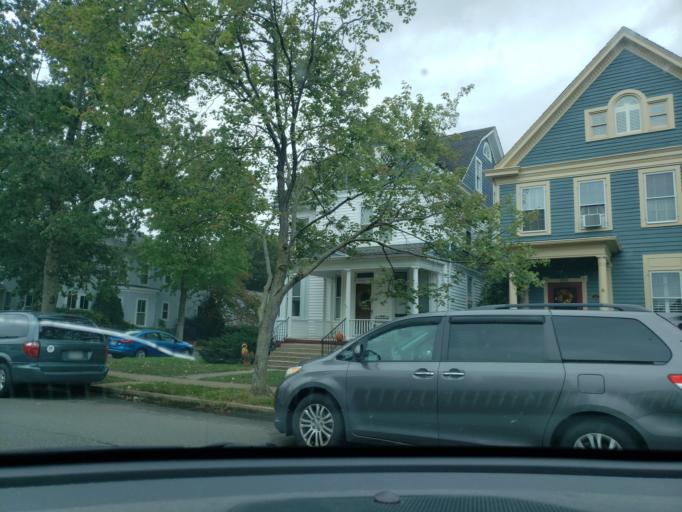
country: US
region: Virginia
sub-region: City of Fredericksburg
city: Fredericksburg
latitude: 38.3045
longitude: -77.4677
